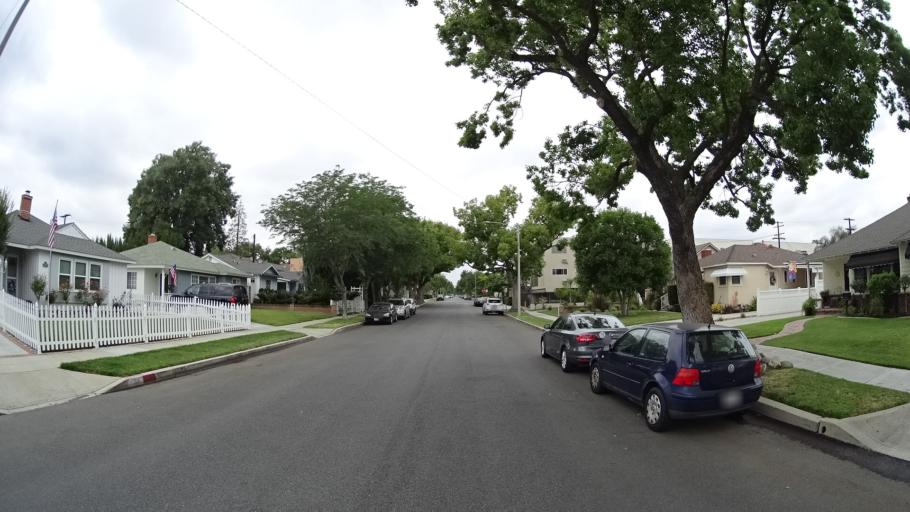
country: US
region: California
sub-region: Los Angeles County
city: Burbank
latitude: 34.1666
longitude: -118.3358
